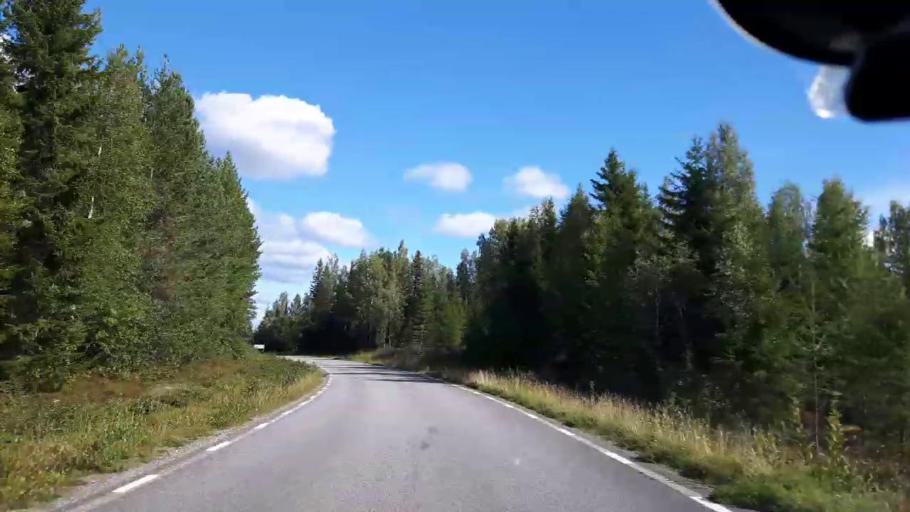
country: SE
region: Jaemtland
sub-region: OEstersunds Kommun
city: Brunflo
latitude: 63.2068
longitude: 15.2460
